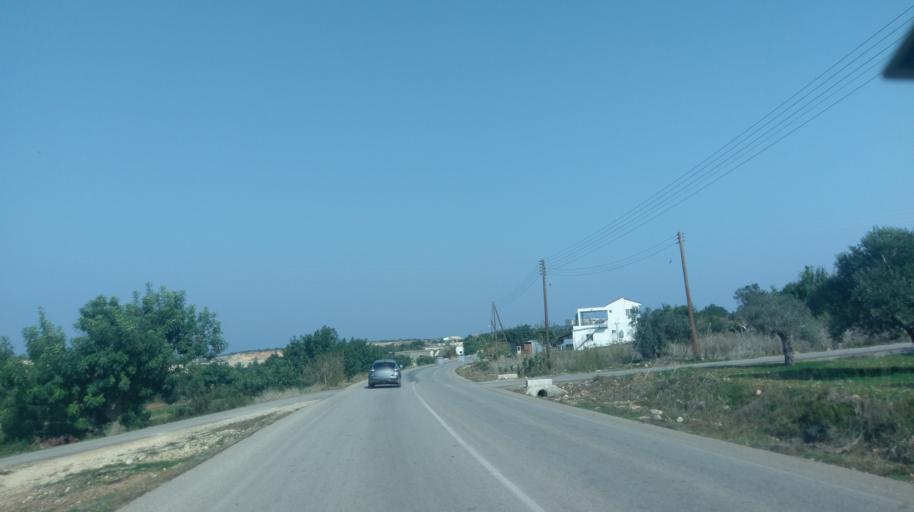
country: CY
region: Ammochostos
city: Leonarisso
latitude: 35.5106
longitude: 34.1612
